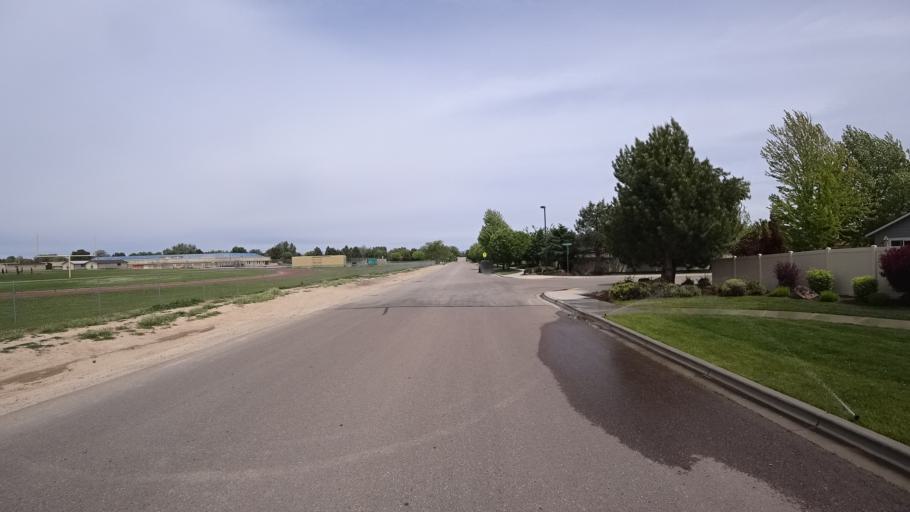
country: US
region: Idaho
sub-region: Ada County
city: Meridian
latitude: 43.5509
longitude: -116.3243
